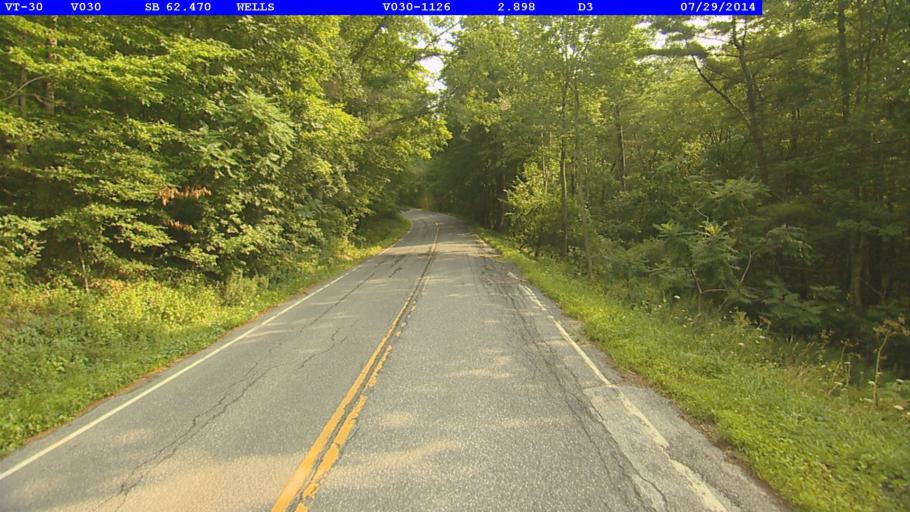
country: US
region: New York
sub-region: Washington County
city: Granville
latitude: 43.4357
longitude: -73.1958
